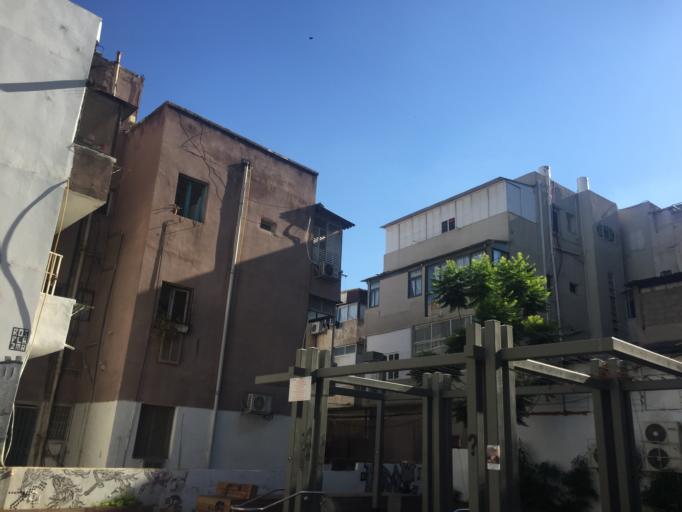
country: IL
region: Tel Aviv
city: Yafo
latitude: 32.0560
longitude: 34.7683
